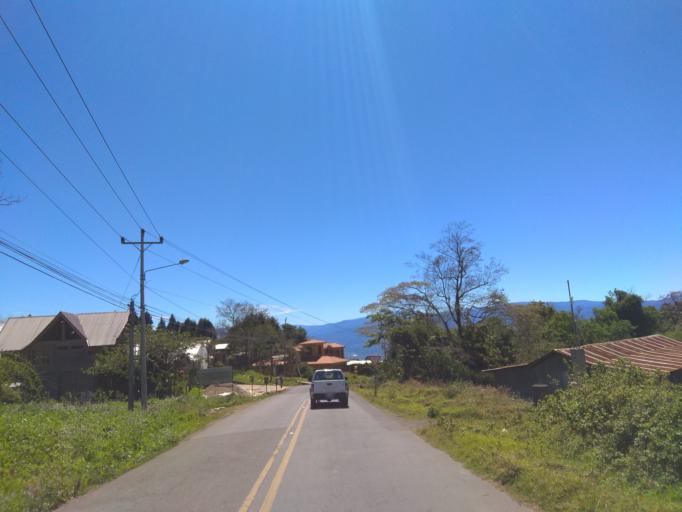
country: CR
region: Cartago
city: Cot
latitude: 9.9201
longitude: -83.9150
